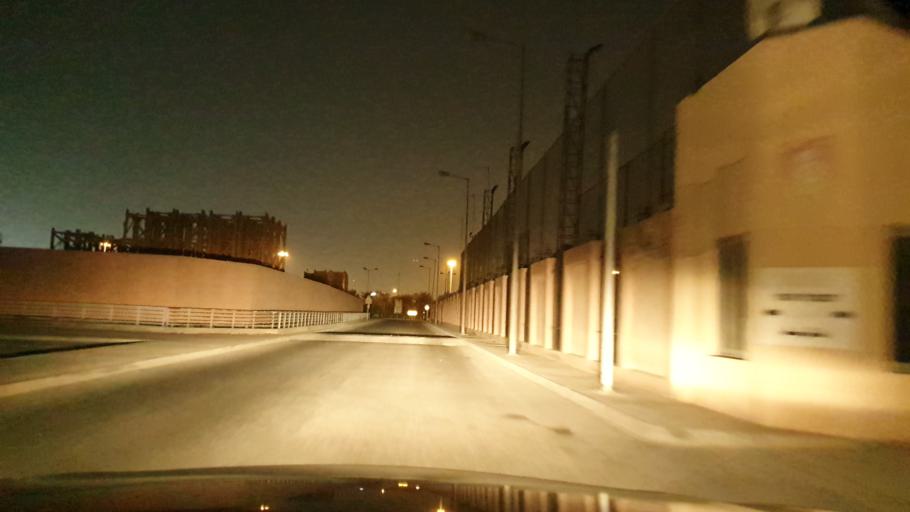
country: BH
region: Manama
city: Jidd Hafs
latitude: 26.1992
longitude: 50.5480
